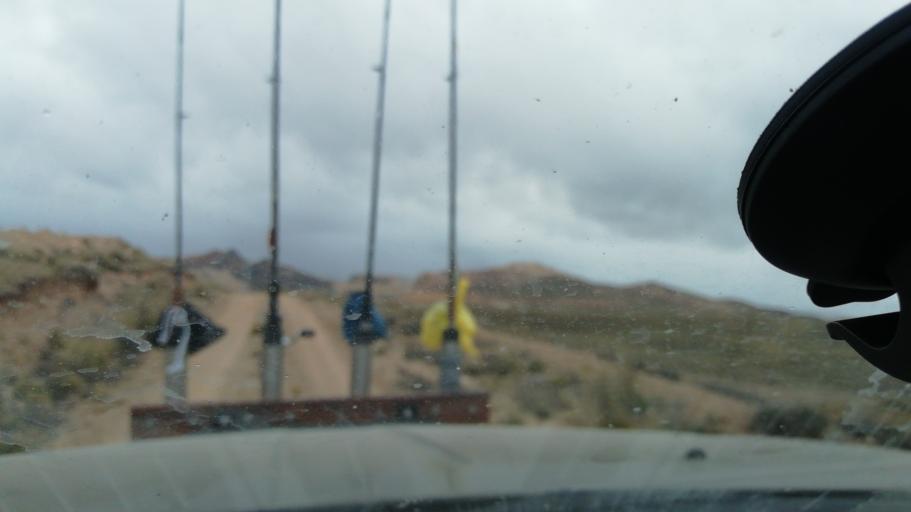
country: PE
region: Huancavelica
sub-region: Provincia de Huancavelica
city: Acobambilla
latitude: -12.5799
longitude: -75.5359
